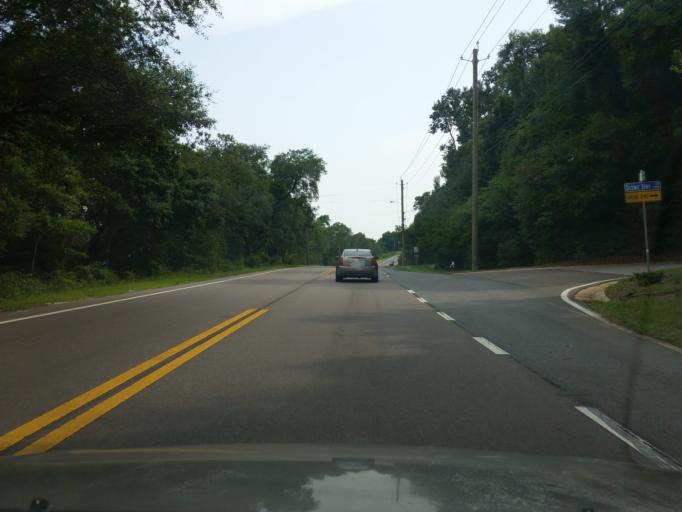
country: US
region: Florida
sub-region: Escambia County
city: East Pensacola Heights
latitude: 30.4658
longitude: -87.1622
